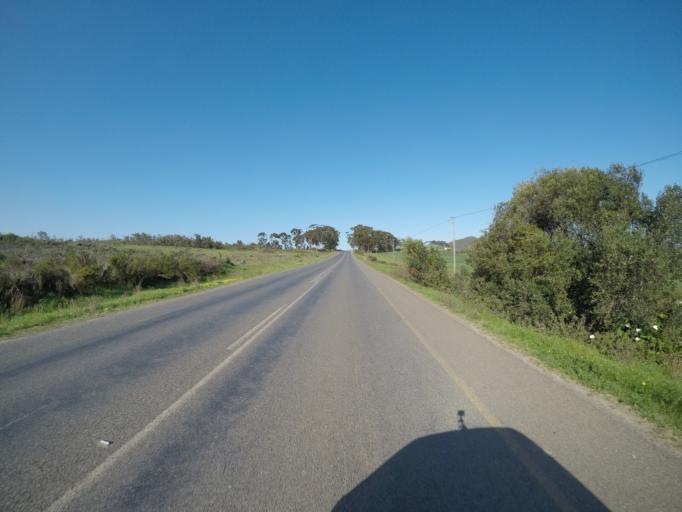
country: ZA
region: Western Cape
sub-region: City of Cape Town
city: Kraaifontein
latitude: -33.7645
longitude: 18.7686
